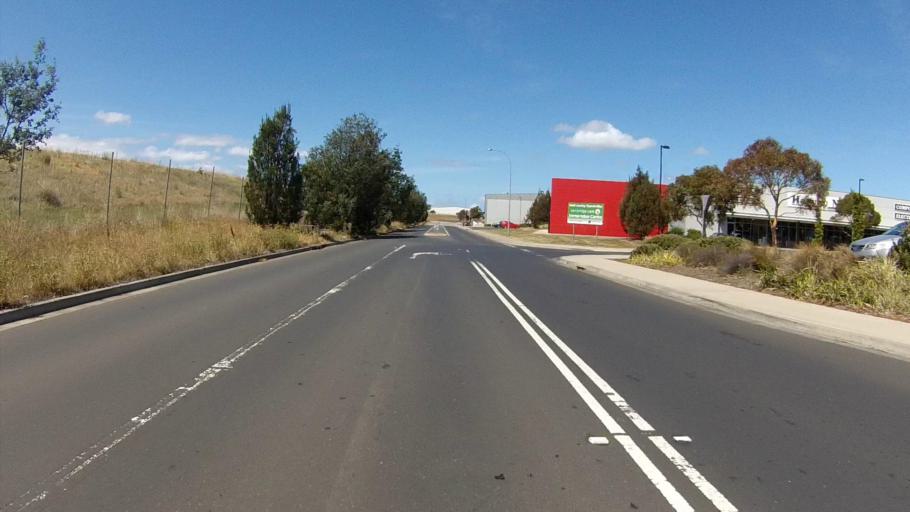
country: AU
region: Tasmania
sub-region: Clarence
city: Cambridge
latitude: -42.8328
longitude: 147.4663
